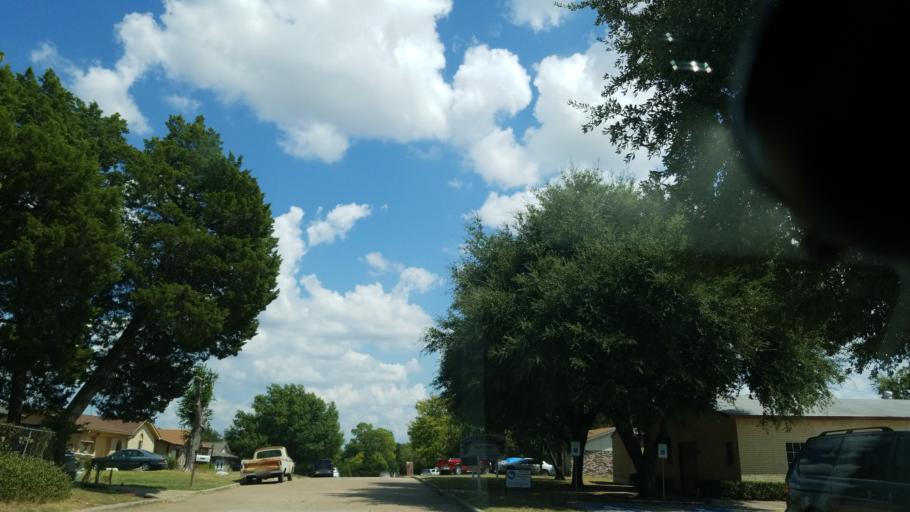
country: US
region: Texas
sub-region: Dallas County
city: Grand Prairie
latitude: 32.7285
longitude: -96.9925
